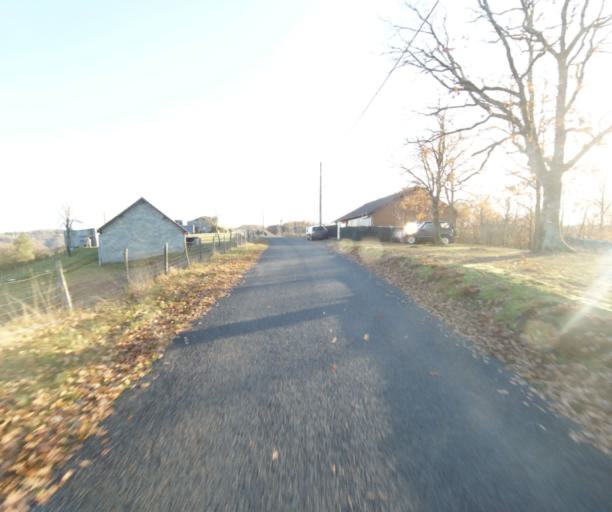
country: FR
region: Limousin
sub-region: Departement de la Correze
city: Laguenne
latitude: 45.2301
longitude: 1.8010
